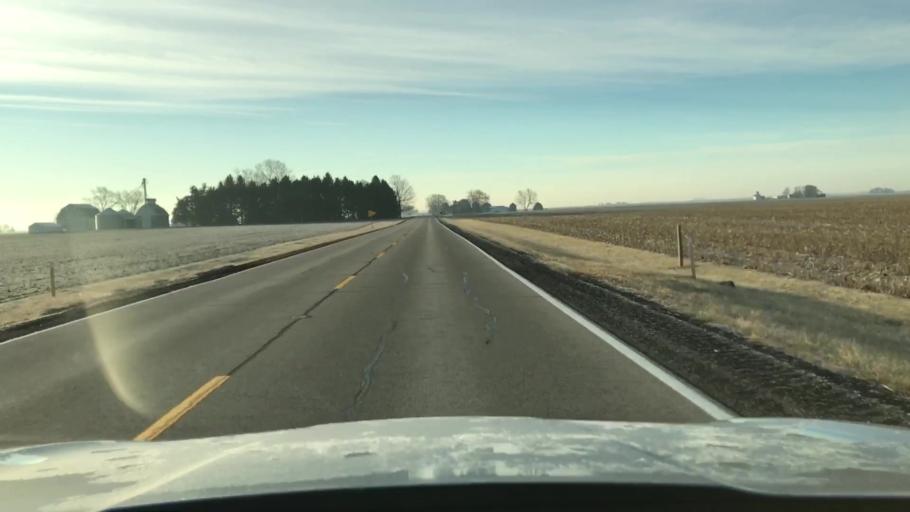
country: US
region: Illinois
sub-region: McLean County
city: Hudson
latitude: 40.6167
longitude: -88.9455
